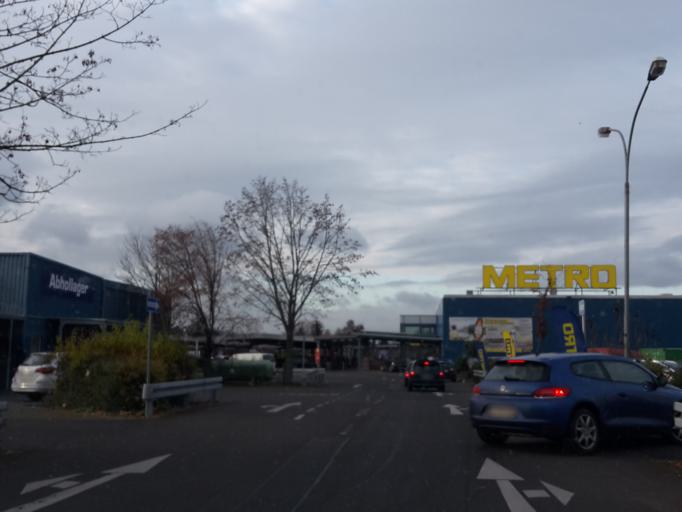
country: DE
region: Rheinland-Pfalz
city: Mainz
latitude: 50.0203
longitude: 8.2911
